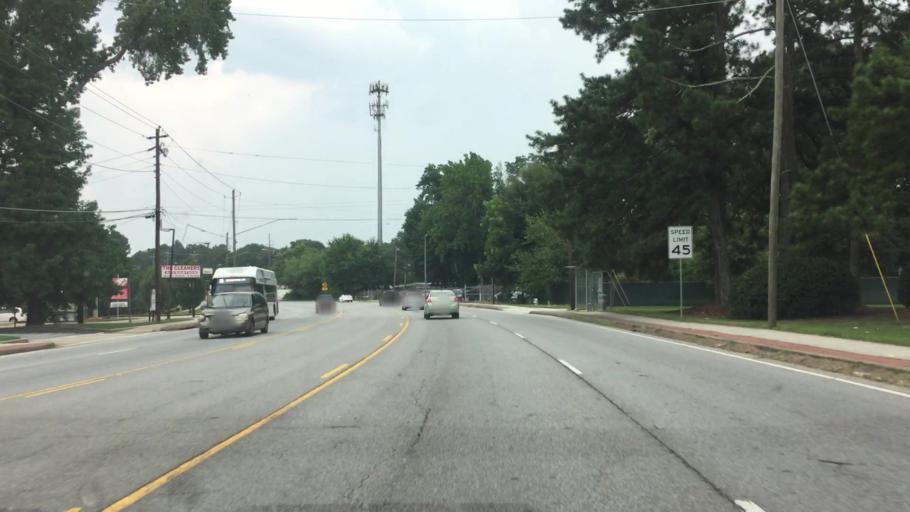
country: US
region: Georgia
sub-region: DeKalb County
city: Avondale Estates
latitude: 33.7636
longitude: -84.2508
